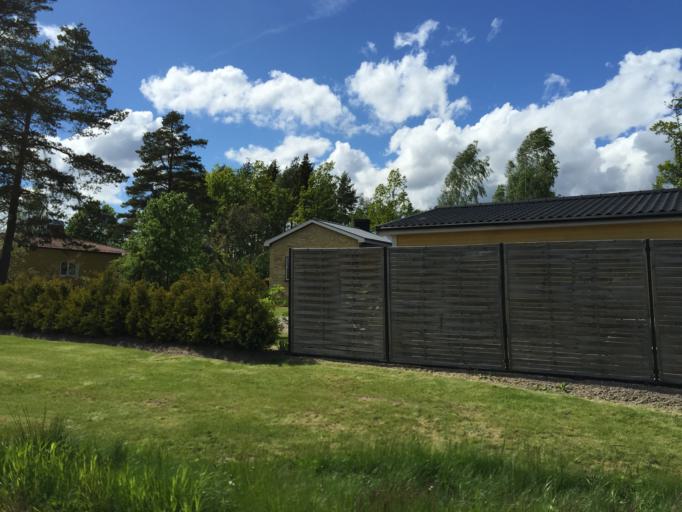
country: SE
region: OEstergoetland
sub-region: Norrkopings Kommun
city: Skarblacka
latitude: 58.5833
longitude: 15.8224
